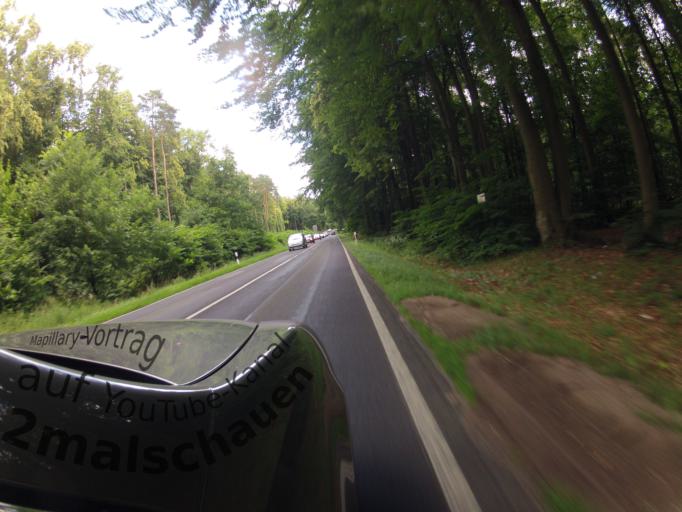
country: DE
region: Mecklenburg-Vorpommern
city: Usedom
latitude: 53.9080
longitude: 14.0199
